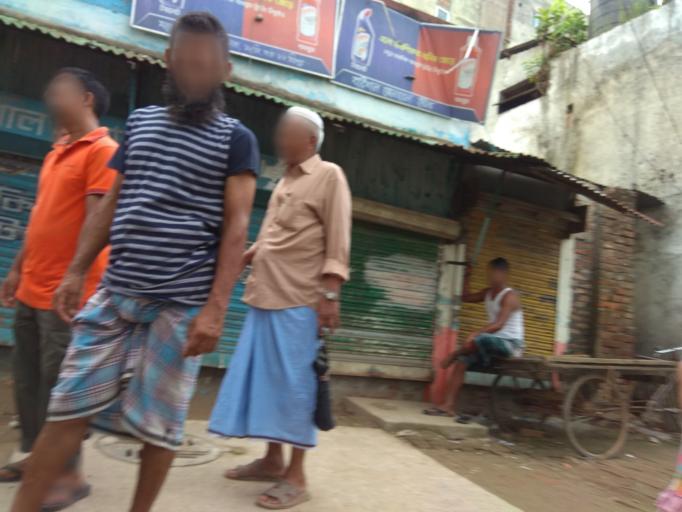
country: BD
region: Dhaka
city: Tungi
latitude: 23.8168
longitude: 90.3757
